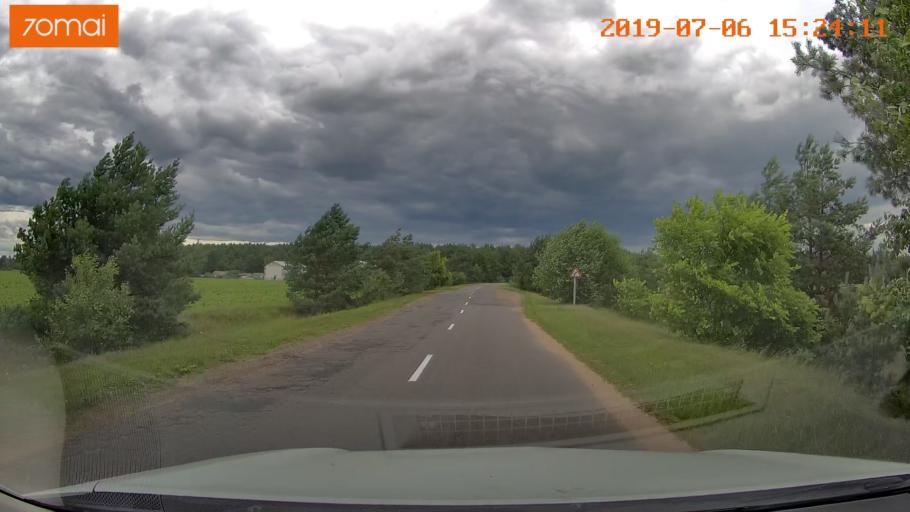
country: BY
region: Minsk
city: Valozhyn
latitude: 54.0177
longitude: 26.6034
